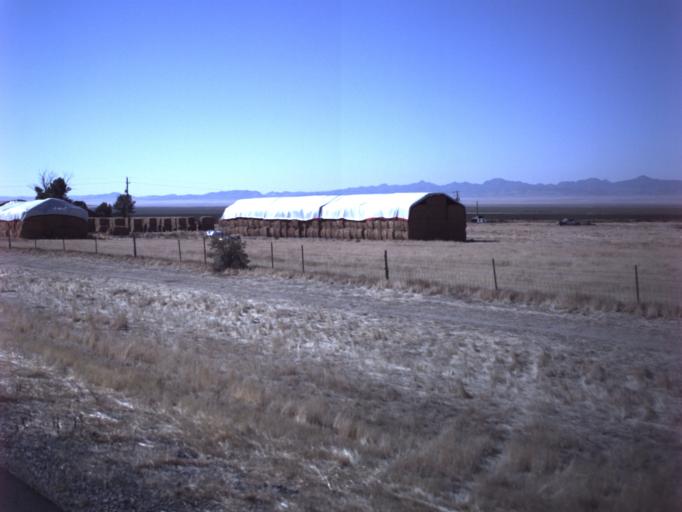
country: US
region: Utah
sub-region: Tooele County
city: Grantsville
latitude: 40.4973
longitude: -112.7481
